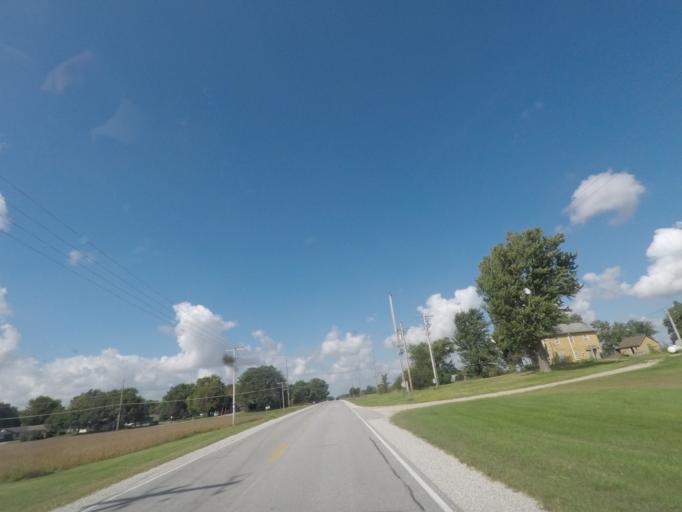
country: US
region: Iowa
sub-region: Story County
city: Nevada
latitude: 42.0225
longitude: -93.3176
